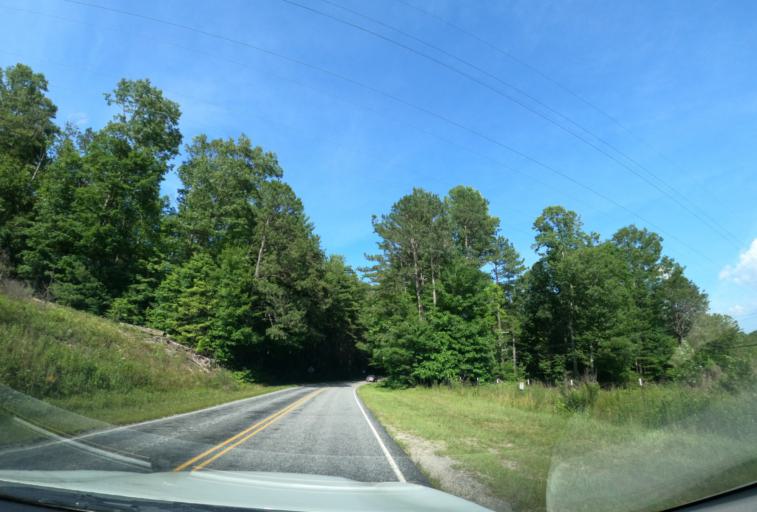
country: US
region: North Carolina
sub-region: Transylvania County
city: Brevard
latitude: 35.1886
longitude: -82.6321
